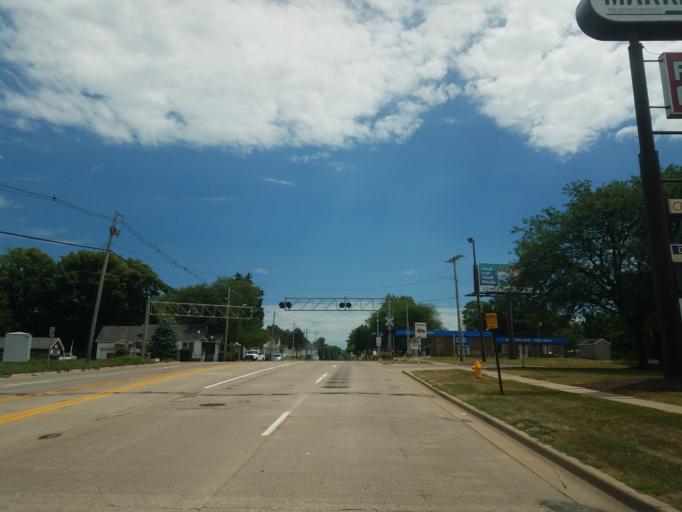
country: US
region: Illinois
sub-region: McLean County
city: Bloomington
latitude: 40.4830
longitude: -89.0150
